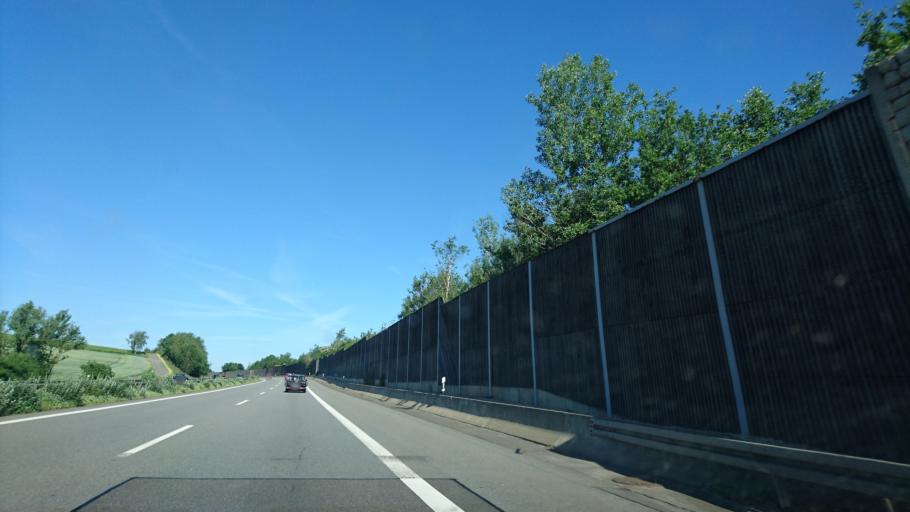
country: DE
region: Saxony
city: Wilkau-Hasslau
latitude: 50.6764
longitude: 12.5508
